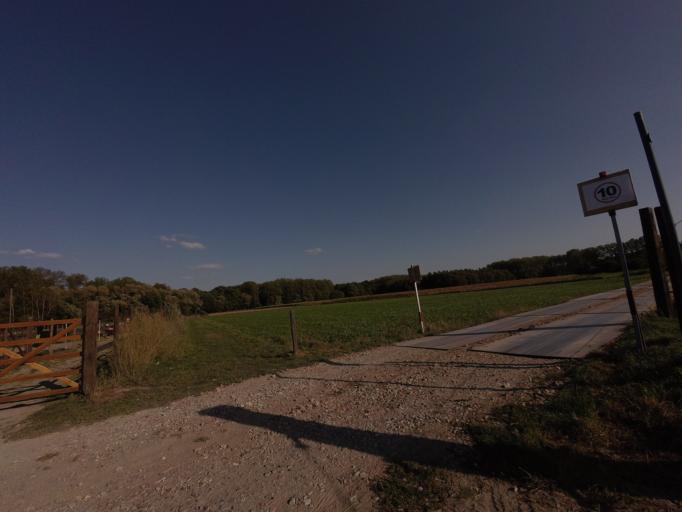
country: BE
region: Flanders
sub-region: Provincie Vlaams-Brabant
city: Kampenhout
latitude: 50.9425
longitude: 4.5777
